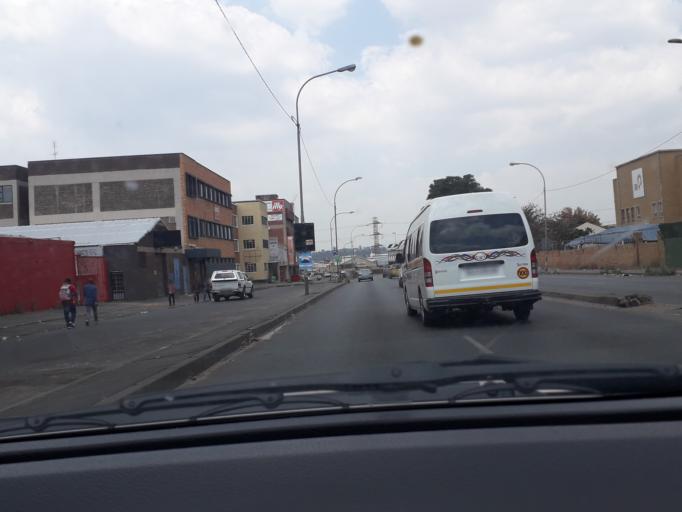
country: ZA
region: Gauteng
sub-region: City of Johannesburg Metropolitan Municipality
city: Johannesburg
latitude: -26.2213
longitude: 28.0436
